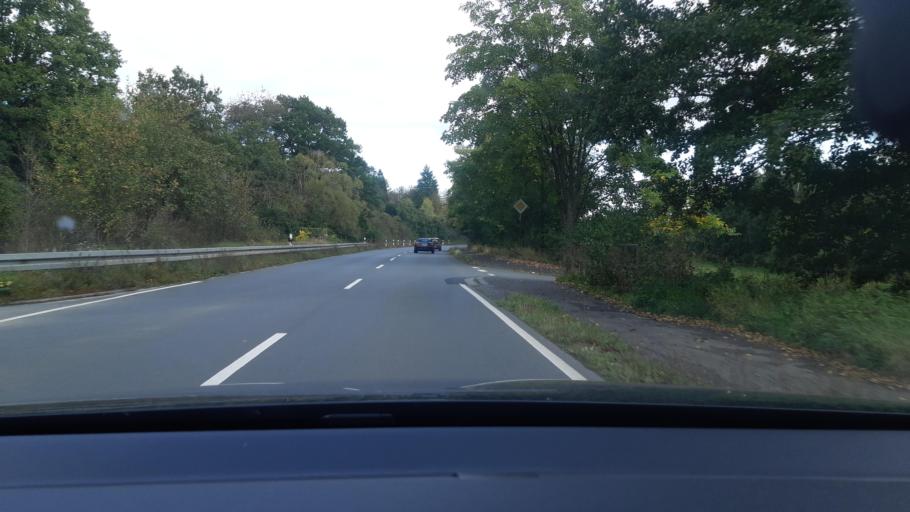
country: DE
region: Hesse
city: Allendorf an der Lahn
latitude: 50.5241
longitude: 8.5684
